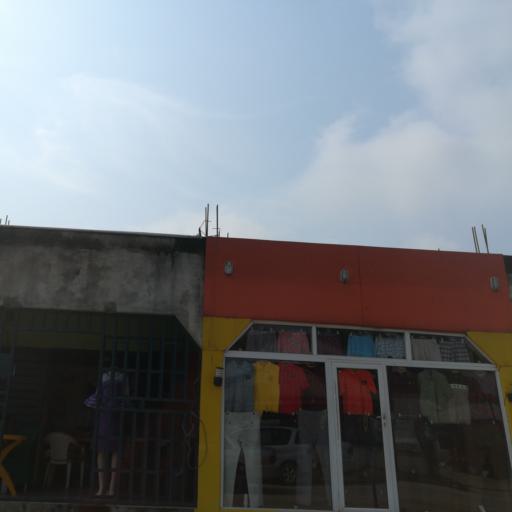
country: NG
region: Rivers
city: Port Harcourt
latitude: 4.8446
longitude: 7.0642
